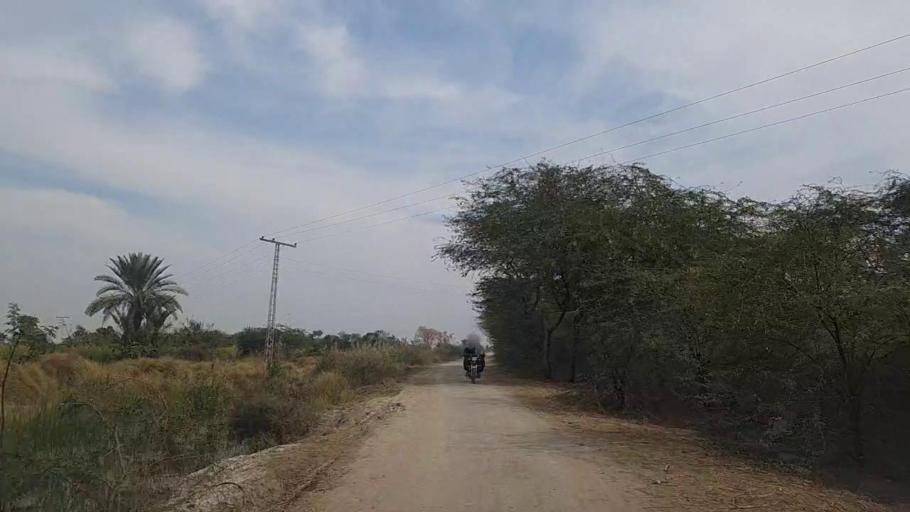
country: PK
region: Sindh
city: Daur
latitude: 26.4993
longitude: 68.3901
